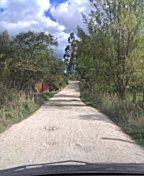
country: CO
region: Boyaca
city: Duitama
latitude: 5.8246
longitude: -73.0793
